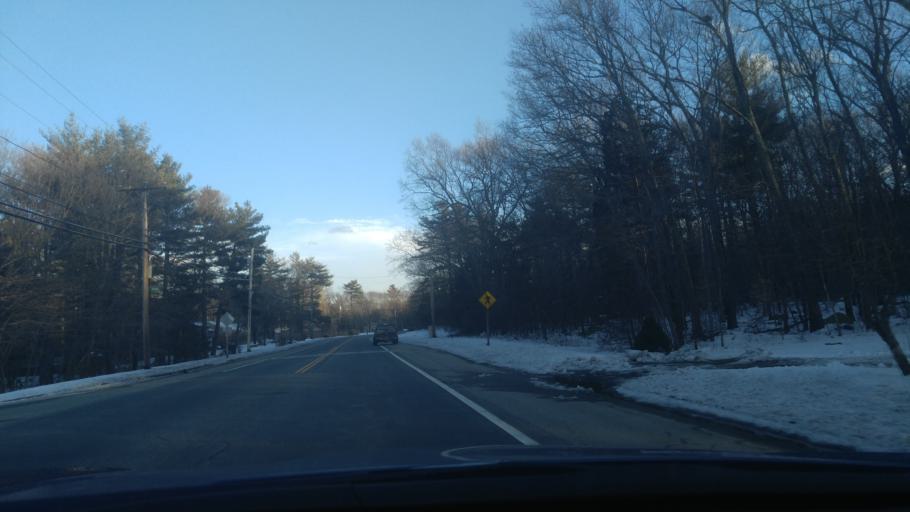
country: US
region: Rhode Island
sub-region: Kent County
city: Coventry
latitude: 41.7103
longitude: -71.6486
